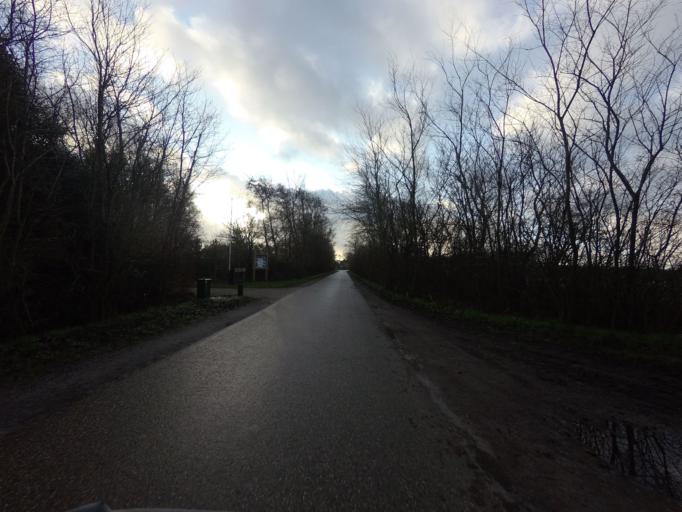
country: NL
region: North Holland
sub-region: Gemeente Texel
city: Den Burg
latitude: 53.0951
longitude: 4.7729
